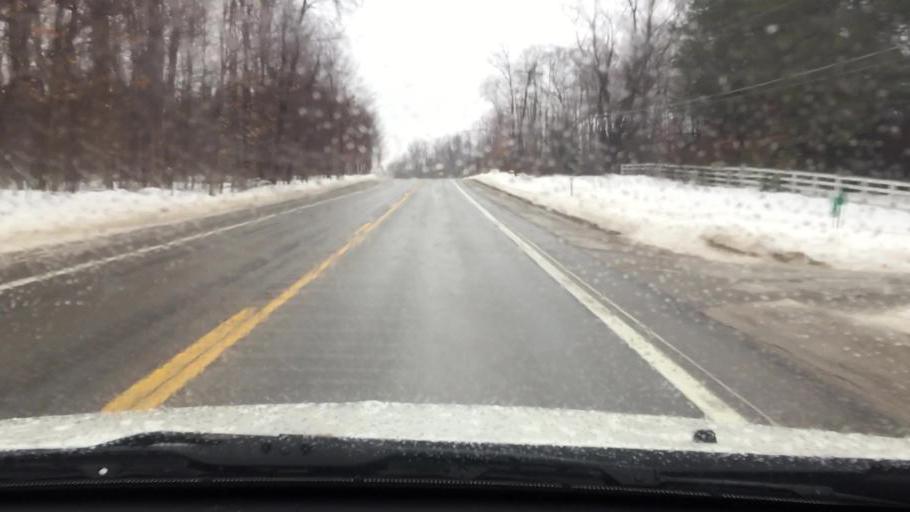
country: US
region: Michigan
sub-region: Charlevoix County
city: East Jordan
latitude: 45.1918
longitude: -85.1644
